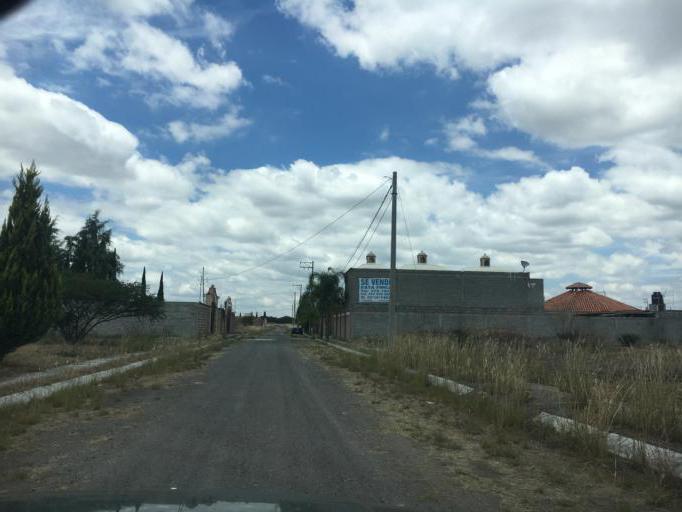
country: MX
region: Guanajuato
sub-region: Leon
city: Plan Guanajuato (La Sandia)
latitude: 20.9257
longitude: -101.7500
